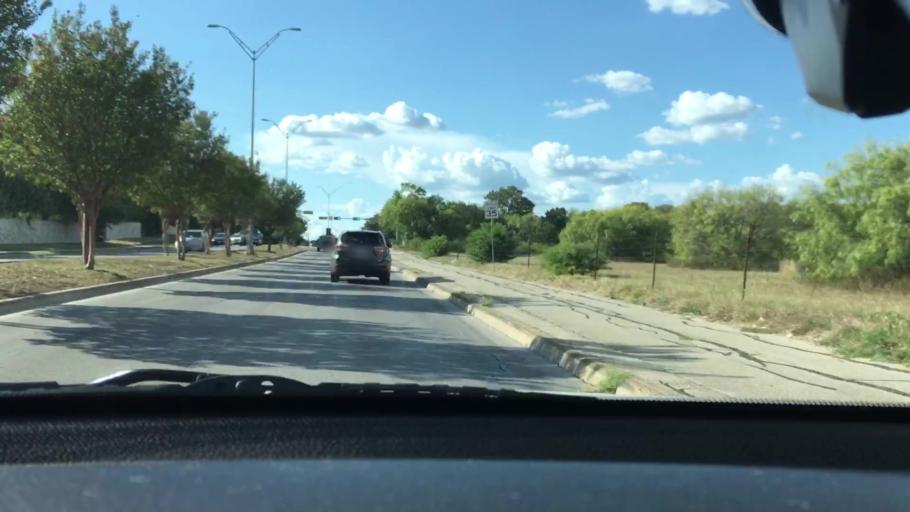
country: US
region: Texas
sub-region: Guadalupe County
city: Schertz
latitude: 29.5724
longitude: -98.2766
